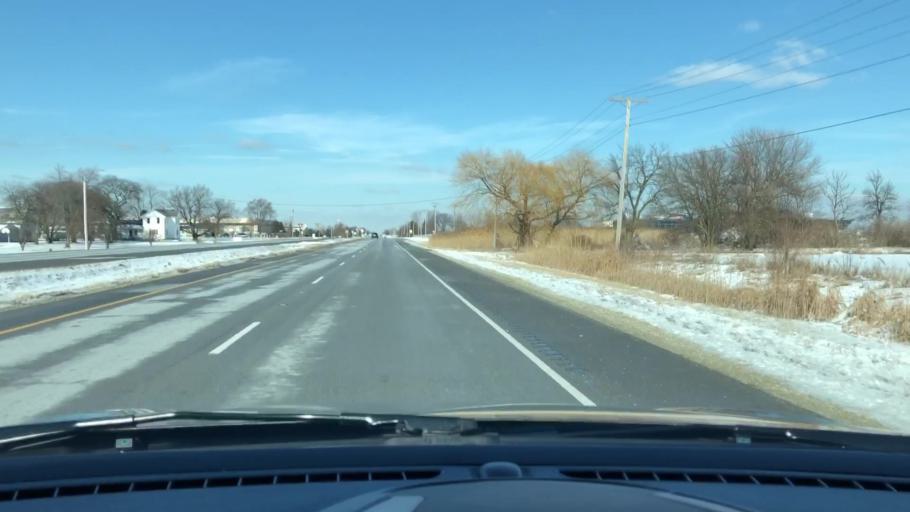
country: US
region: Illinois
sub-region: Will County
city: Preston Heights
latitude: 41.4568
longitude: -88.0792
